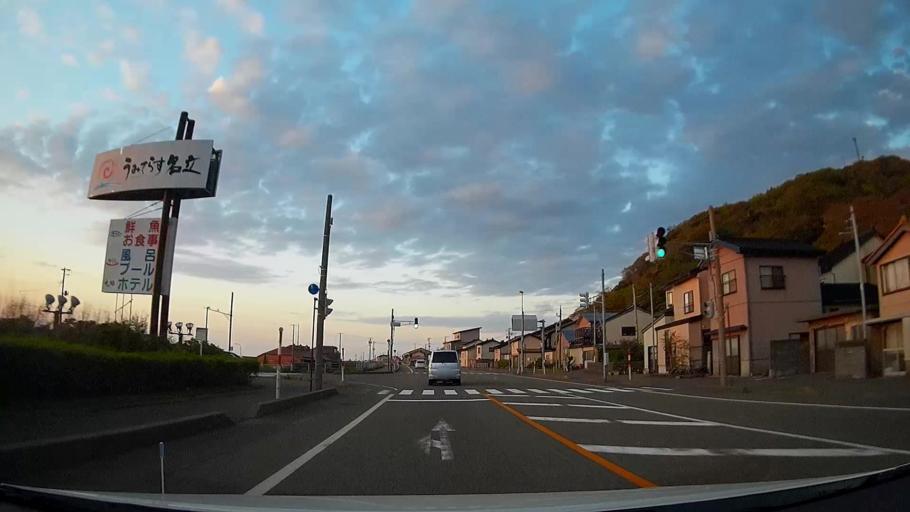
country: JP
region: Niigata
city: Joetsu
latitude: 37.1638
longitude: 138.0879
